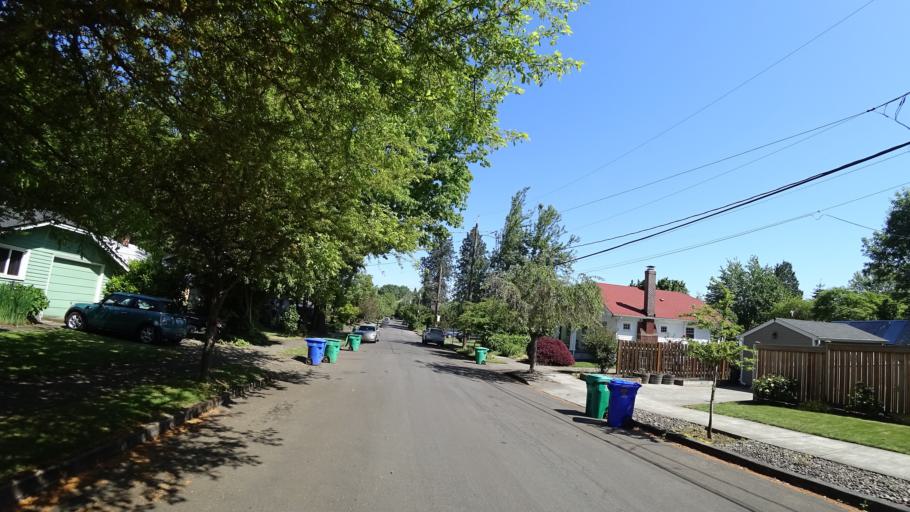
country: US
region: Oregon
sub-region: Multnomah County
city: Lents
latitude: 45.4850
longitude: -122.6124
